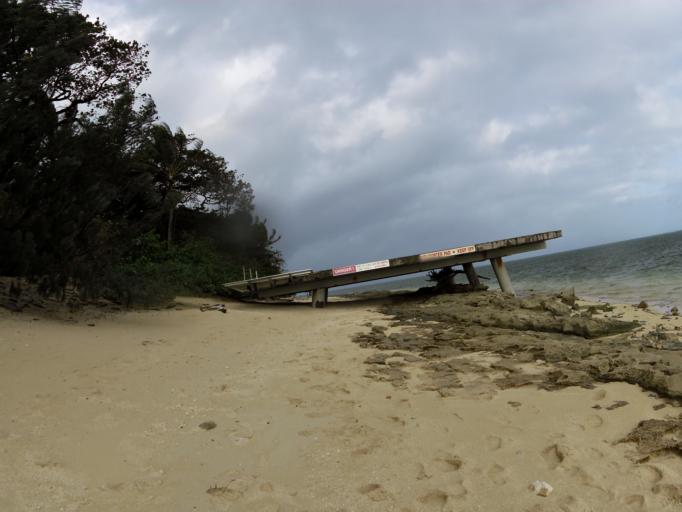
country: AU
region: Queensland
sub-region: Cairns
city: Yorkeys Knob
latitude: -16.7602
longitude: 145.9717
